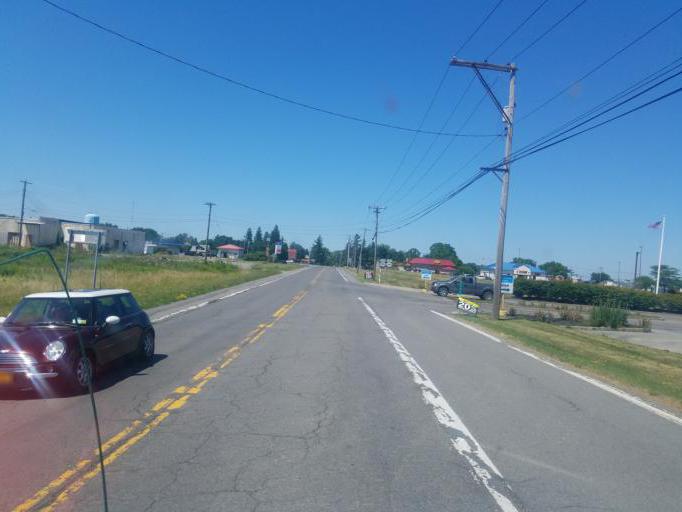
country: US
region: New York
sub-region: Ontario County
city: Geneva
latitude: 42.8545
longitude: -77.0142
